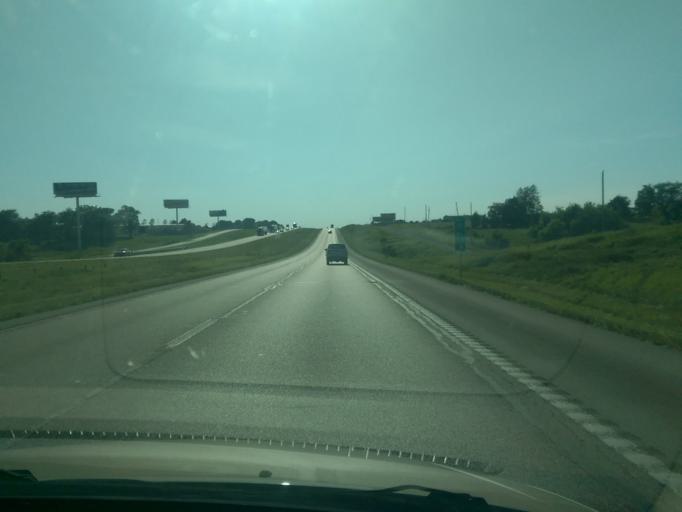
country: US
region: Missouri
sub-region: Lafayette County
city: Odessa
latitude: 39.0098
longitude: -94.0097
